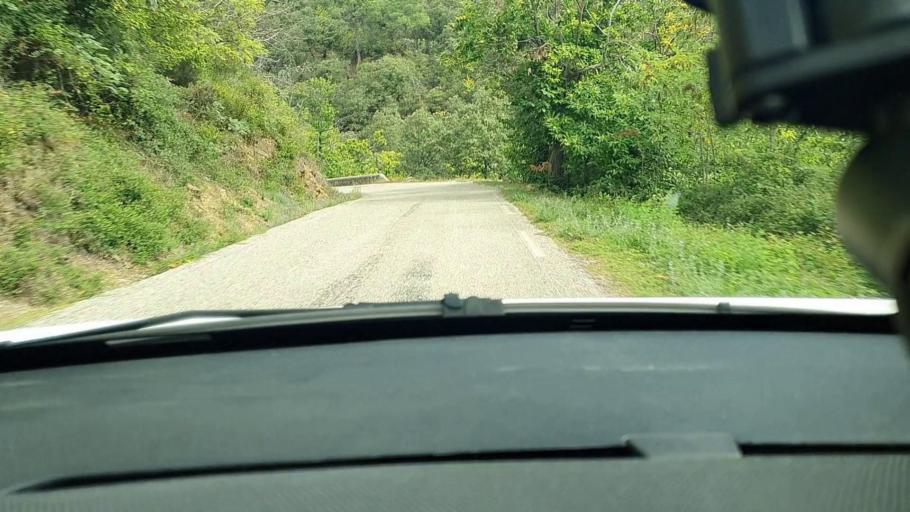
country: FR
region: Languedoc-Roussillon
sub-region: Departement du Gard
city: Branoux-les-Taillades
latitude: 44.2780
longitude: 3.9767
